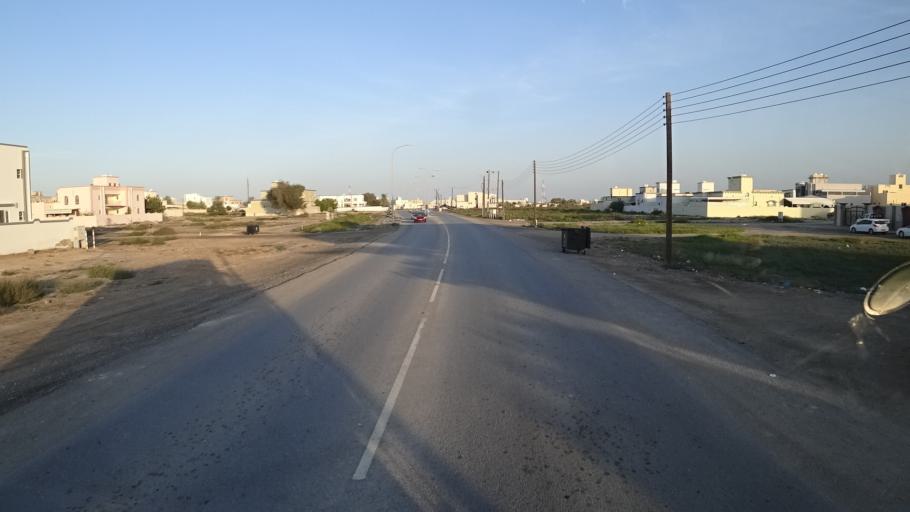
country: OM
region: Al Batinah
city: Barka'
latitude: 23.7043
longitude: 57.9102
